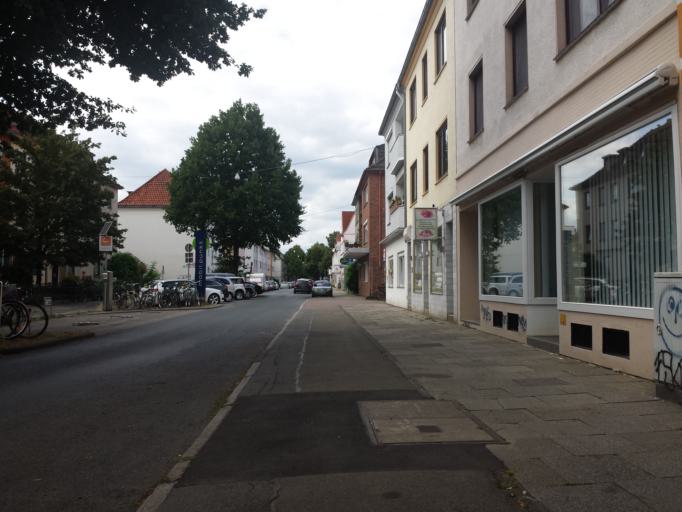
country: DE
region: Bremen
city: Bremen
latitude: 53.0637
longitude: 8.7940
